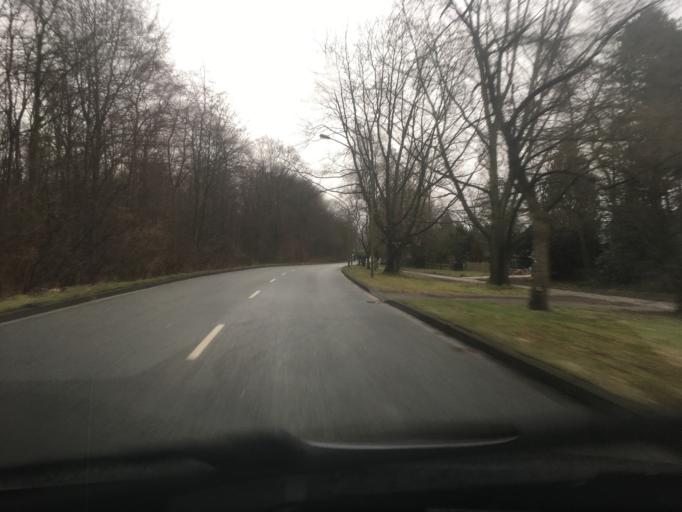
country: DE
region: North Rhine-Westphalia
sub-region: Regierungsbezirk Dusseldorf
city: Dinslaken
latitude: 51.5614
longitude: 6.8207
